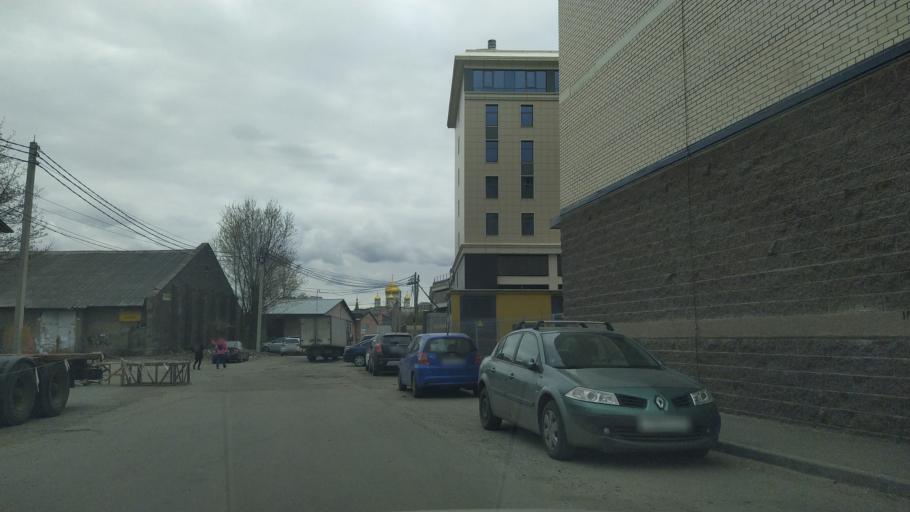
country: RU
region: St.-Petersburg
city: Saint Petersburg
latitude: 59.9023
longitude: 30.3264
